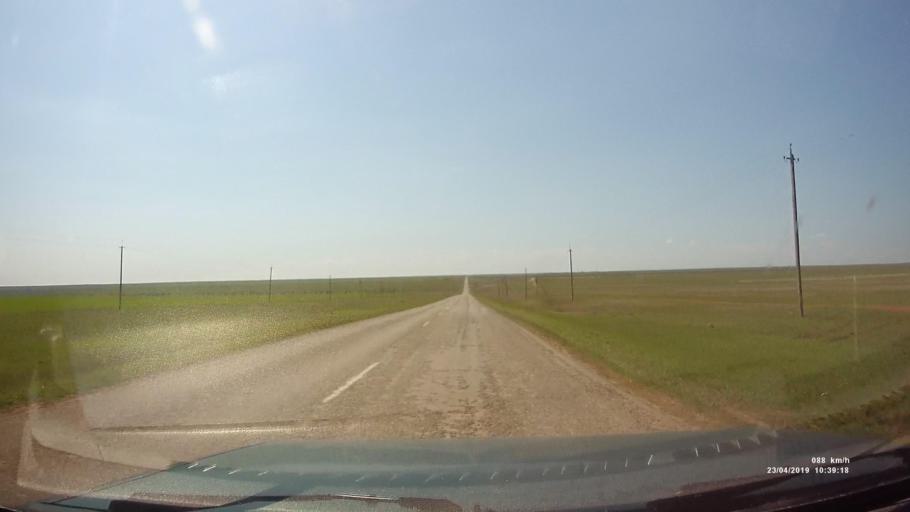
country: RU
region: Kalmykiya
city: Yashalta
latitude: 46.5210
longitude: 42.6387
